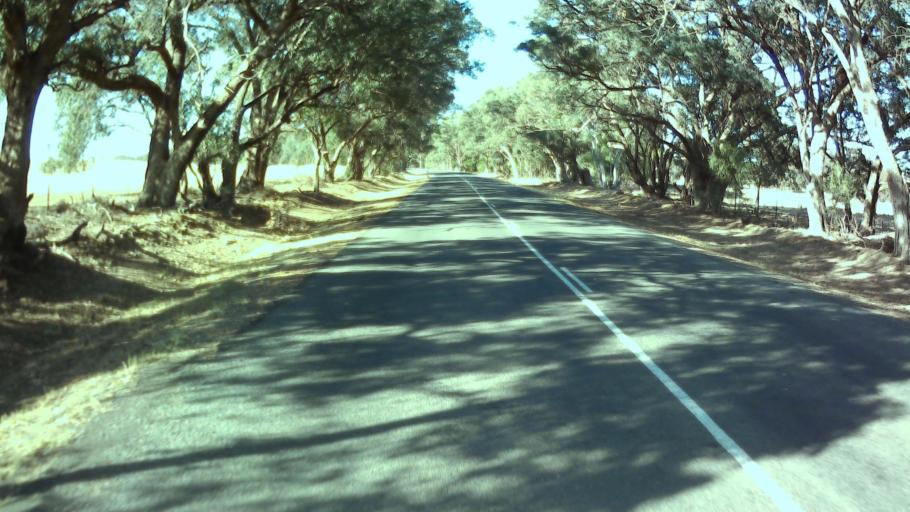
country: AU
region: New South Wales
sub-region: Weddin
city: Grenfell
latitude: -33.9923
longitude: 148.1350
